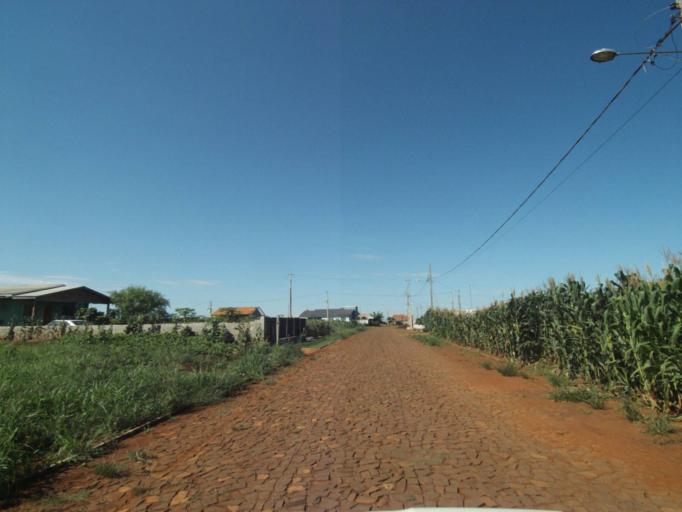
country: BR
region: Parana
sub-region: Laranjeiras Do Sul
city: Laranjeiras do Sul
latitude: -25.4843
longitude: -52.5236
